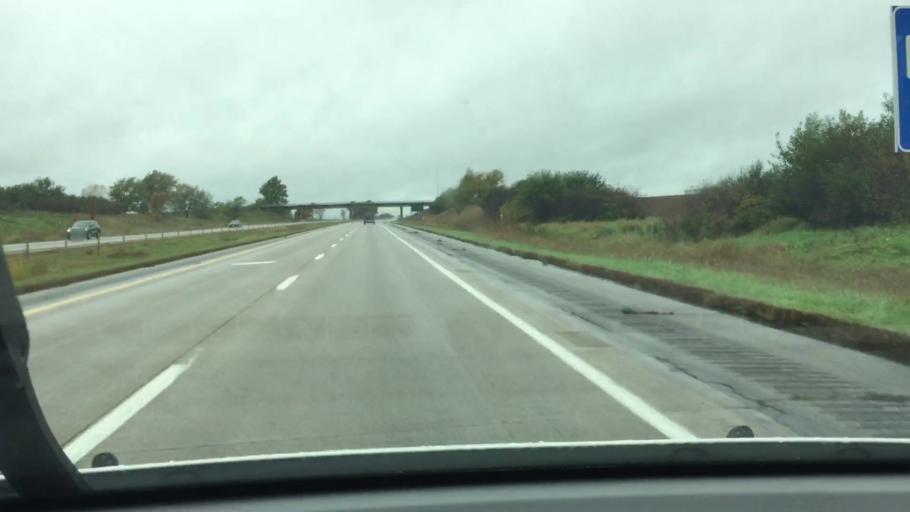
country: US
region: Iowa
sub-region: Jasper County
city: Newton
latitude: 41.6803
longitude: -92.9376
